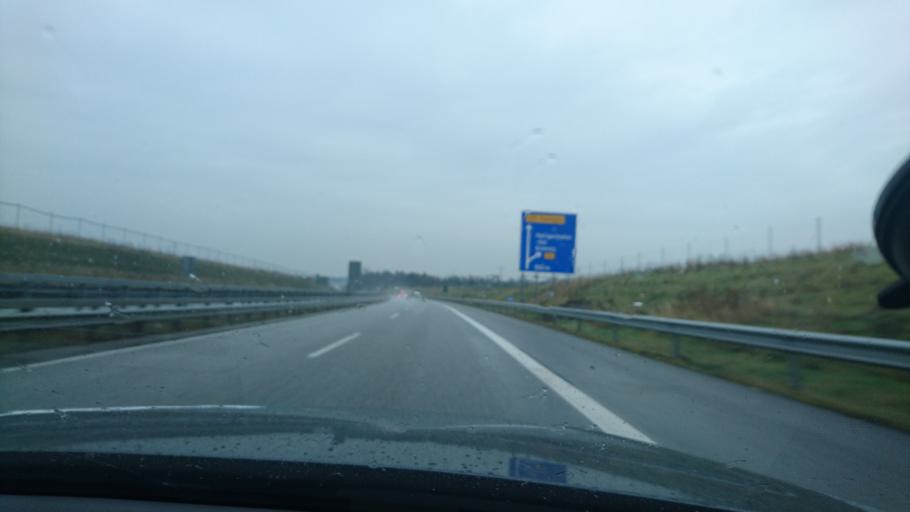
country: DE
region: Schleswig-Holstein
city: Heiligenhafen
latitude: 54.3615
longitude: 10.9996
